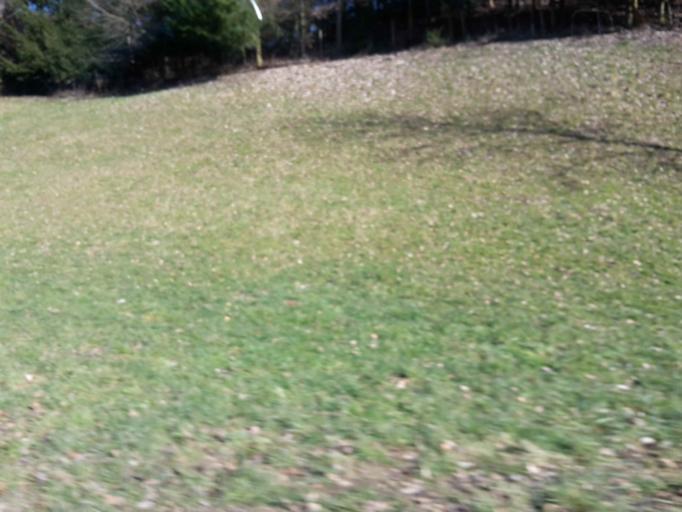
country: CH
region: Bern
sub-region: Emmental District
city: Durrenroth
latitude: 47.1076
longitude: 7.7760
